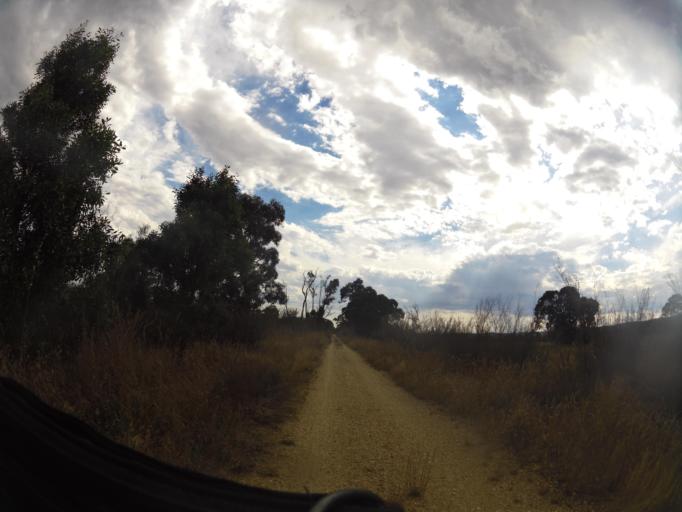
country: AU
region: Victoria
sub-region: Wellington
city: Heyfield
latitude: -38.0409
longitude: 146.6461
